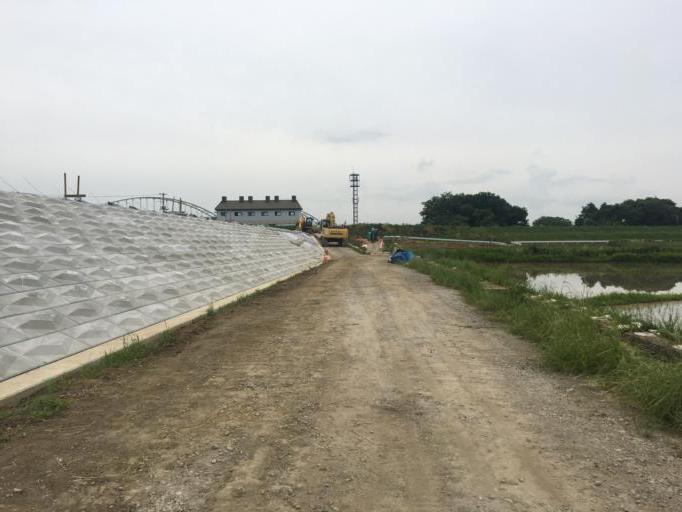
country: JP
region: Saitama
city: Sakado
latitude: 36.0123
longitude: 139.4399
